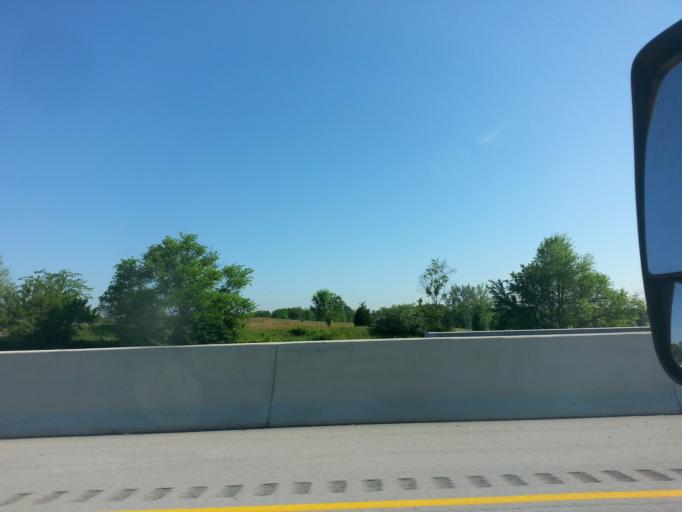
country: US
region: Kentucky
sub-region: Shelby County
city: Simpsonville
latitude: 38.2089
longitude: -85.3558
